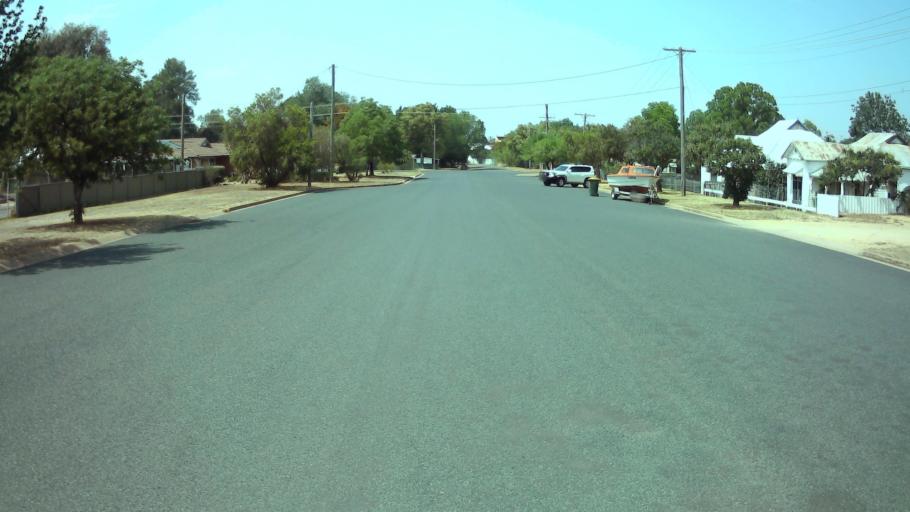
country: AU
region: New South Wales
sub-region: Weddin
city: Grenfell
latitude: -33.8909
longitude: 148.1588
